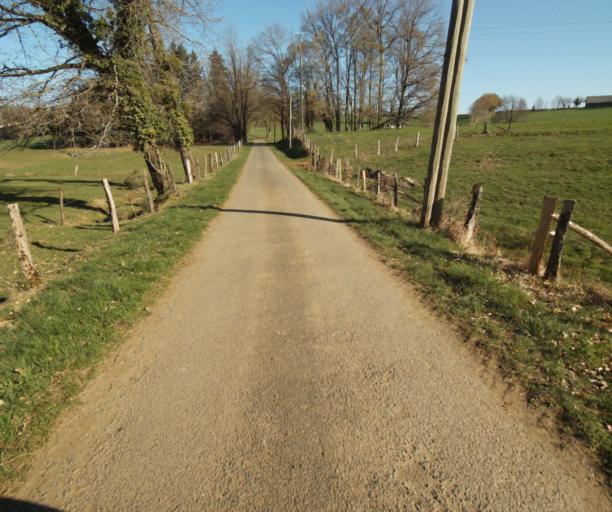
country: FR
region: Limousin
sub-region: Departement de la Correze
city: Saint-Clement
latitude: 45.3793
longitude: 1.6544
